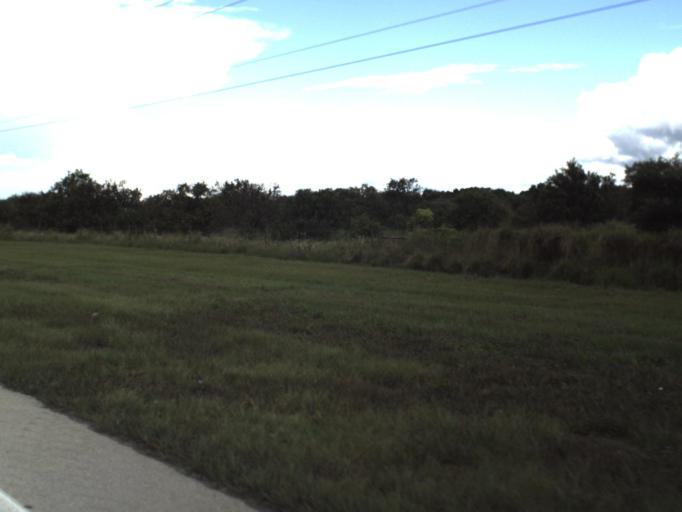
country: US
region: Florida
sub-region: Polk County
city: Mulberry
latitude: 27.7484
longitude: -81.9961
